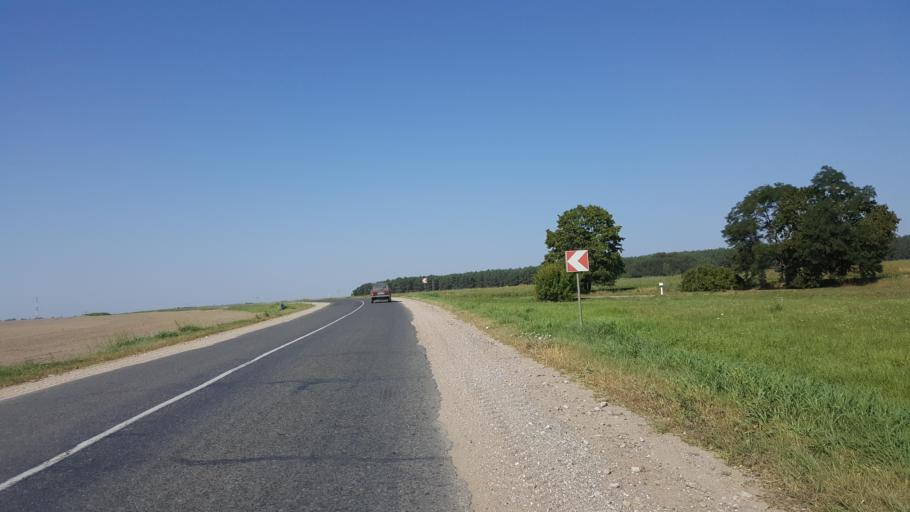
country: BY
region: Brest
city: Kamyanyets
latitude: 52.4176
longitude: 23.6584
